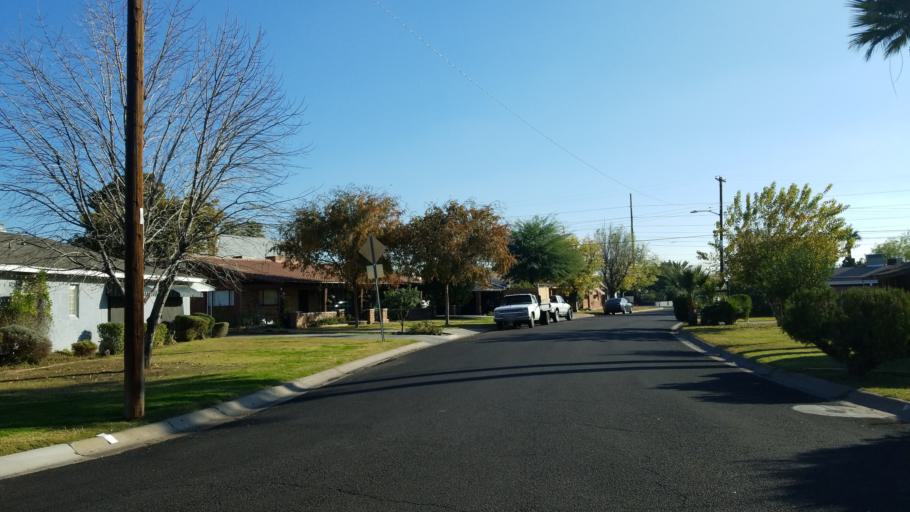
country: US
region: Arizona
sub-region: Maricopa County
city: Phoenix
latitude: 33.4775
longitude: -112.0532
